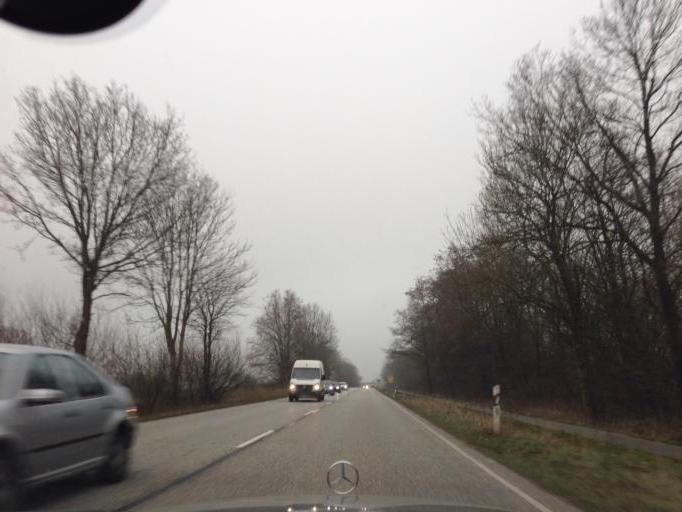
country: DE
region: Schleswig-Holstein
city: Klein Barkau
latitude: 54.2305
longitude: 10.1463
